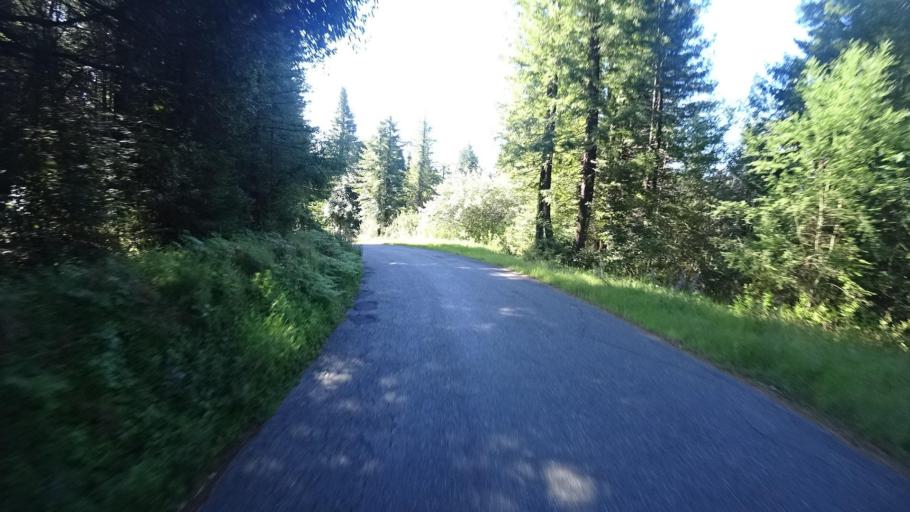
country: US
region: California
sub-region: Humboldt County
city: Rio Dell
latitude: 40.4448
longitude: -123.9753
